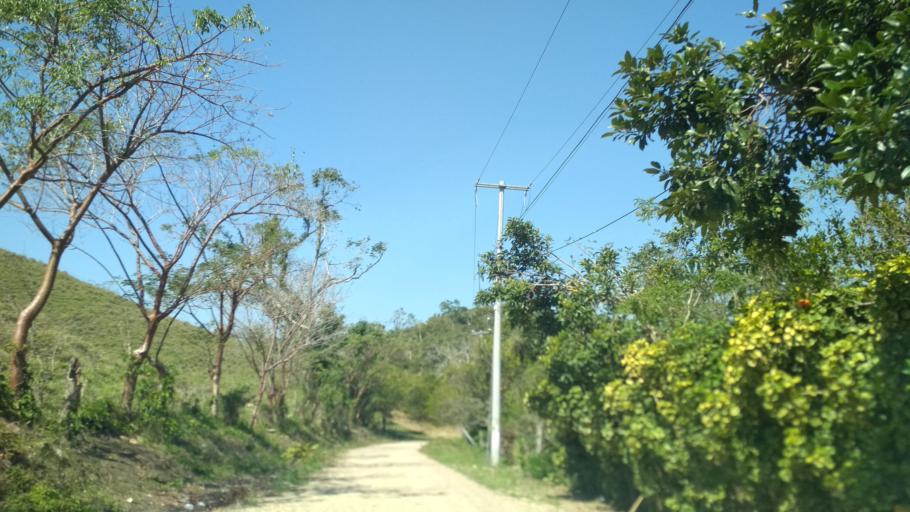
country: MX
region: Veracruz
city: Gutierrez Zamora
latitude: 20.4896
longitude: -97.1654
